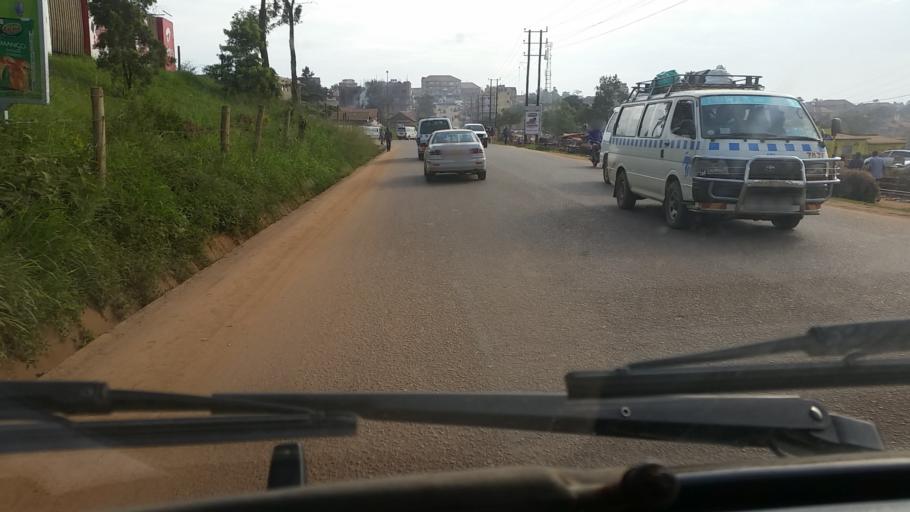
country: UG
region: Central Region
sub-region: Wakiso District
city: Bweyogerere
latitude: 0.3486
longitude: 32.6616
